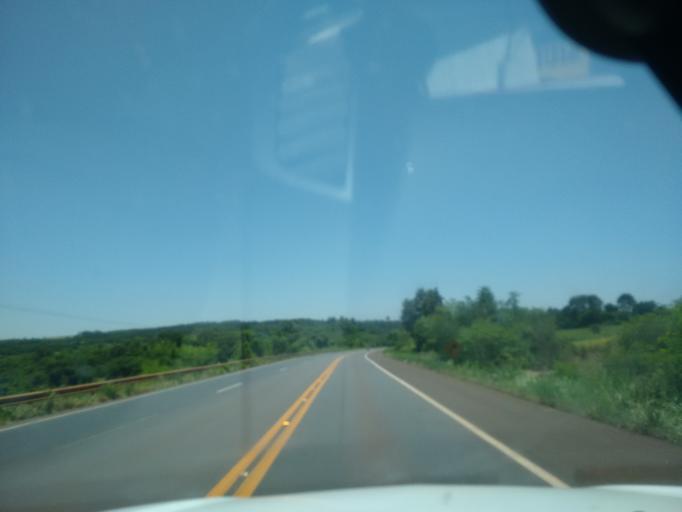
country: BR
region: Parana
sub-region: Marechal Candido Rondon
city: Marechal Candido Rondon
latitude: -24.4238
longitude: -54.1668
